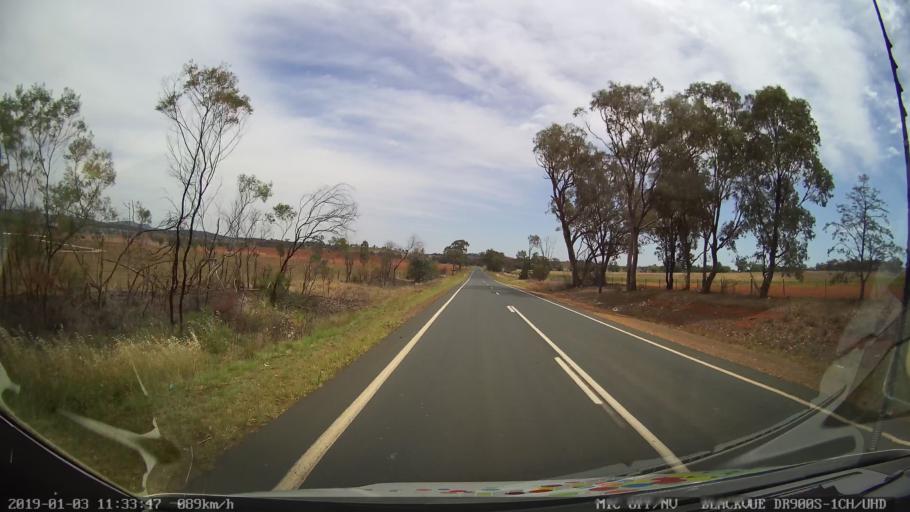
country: AU
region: New South Wales
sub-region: Weddin
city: Grenfell
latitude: -33.9427
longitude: 148.1684
